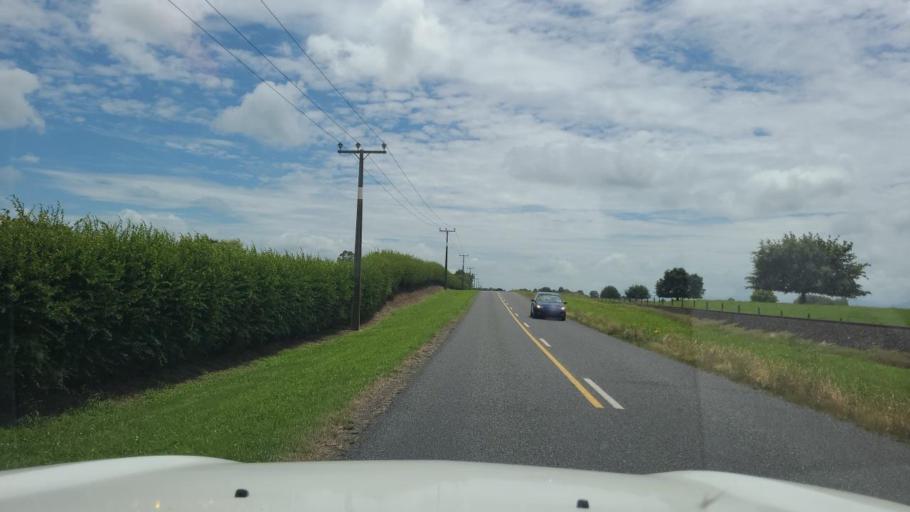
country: NZ
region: Waikato
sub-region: Matamata-Piako District
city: Matamata
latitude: -37.8709
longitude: 175.7564
